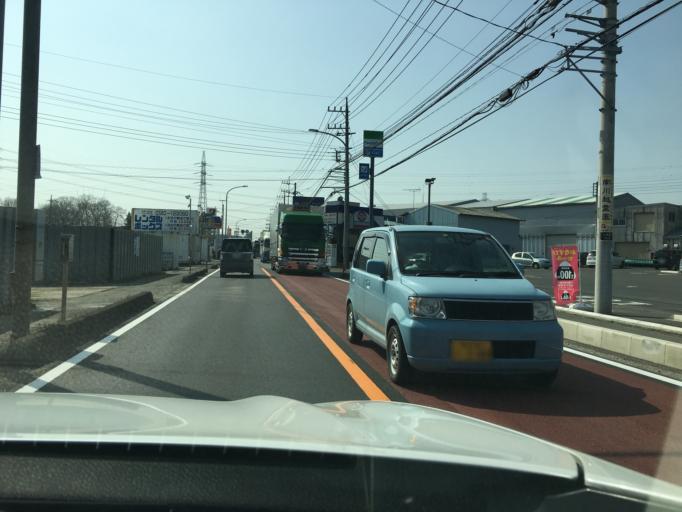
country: JP
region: Saitama
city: Tokorozawa
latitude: 35.8470
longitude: 139.4671
